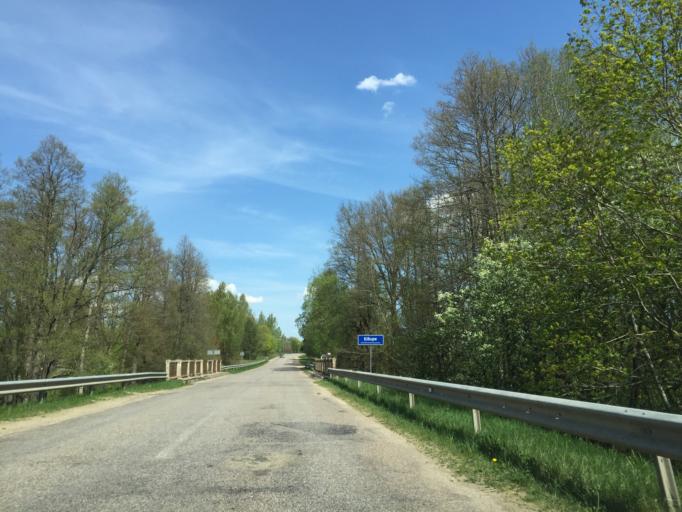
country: LV
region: Krimulda
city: Ragana
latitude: 57.3257
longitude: 24.6401
